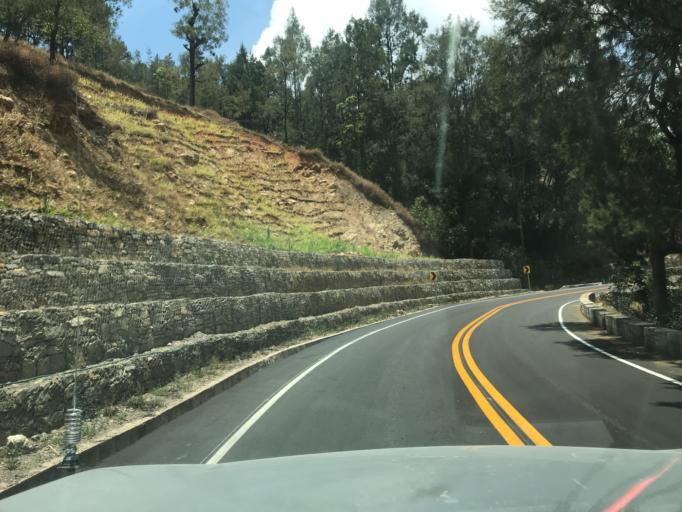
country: TL
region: Manufahi
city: Same
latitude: -8.8760
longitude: 125.5917
